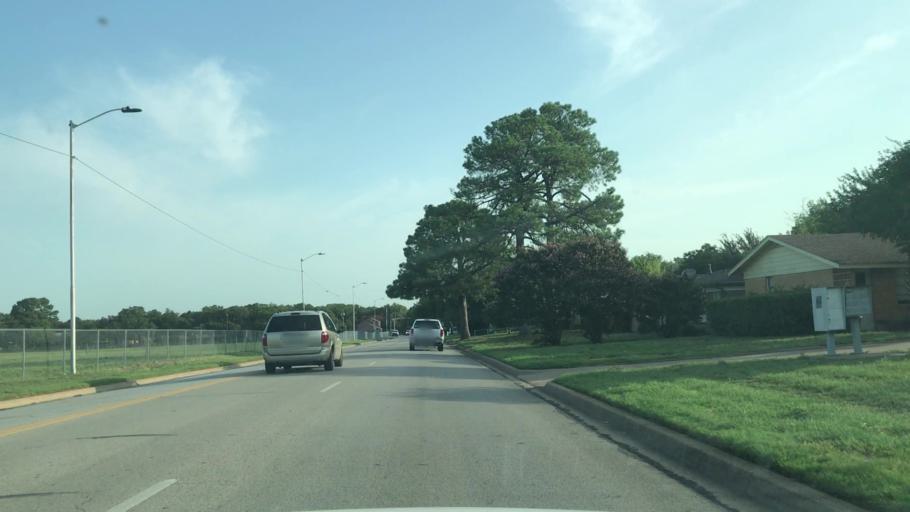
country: US
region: Texas
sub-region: Tarrant County
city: Arlington
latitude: 32.7401
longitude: -97.1233
